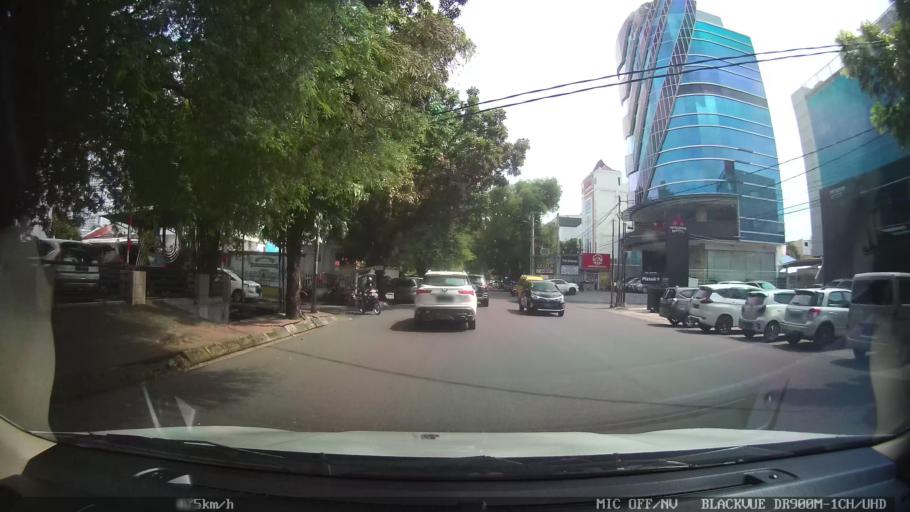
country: ID
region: North Sumatra
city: Medan
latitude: 3.5980
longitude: 98.6690
